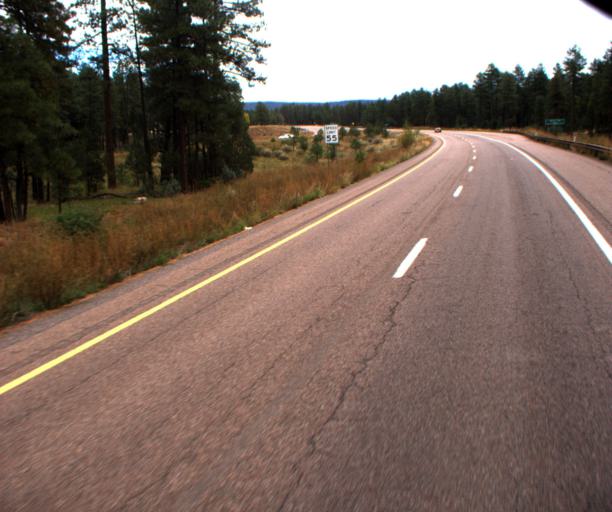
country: US
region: Arizona
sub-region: Gila County
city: Star Valley
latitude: 34.2944
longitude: -110.9798
